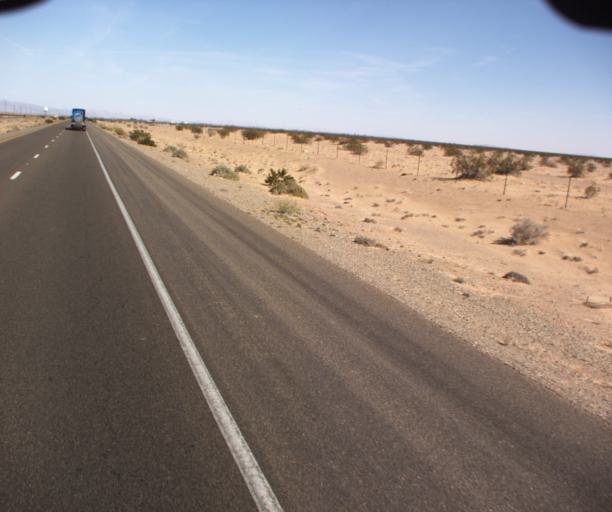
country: MX
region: Sonora
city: San Luis Rio Colorado
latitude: 32.4945
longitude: -114.6777
